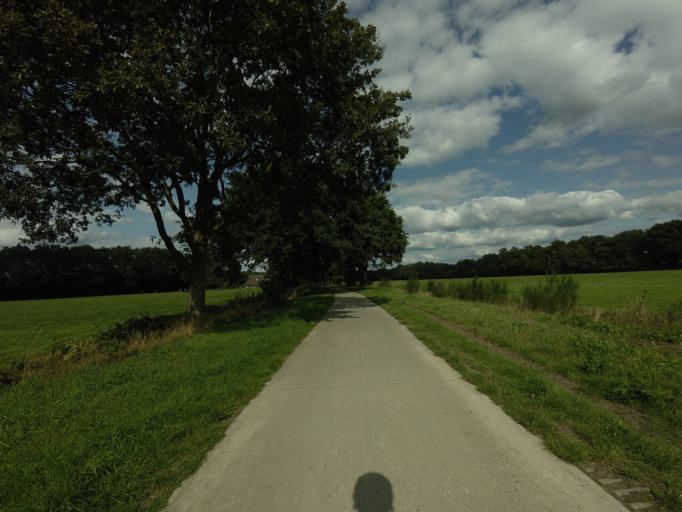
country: NL
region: Drenthe
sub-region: Gemeente De Wolden
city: Ruinen
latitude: 52.7991
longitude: 6.3460
